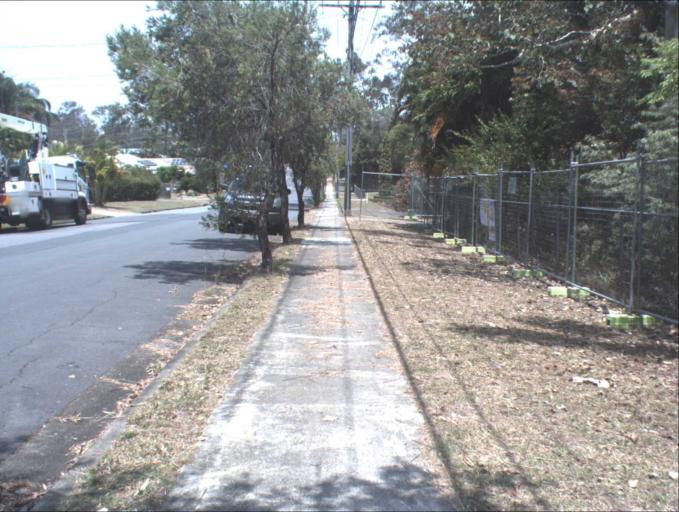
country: AU
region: Queensland
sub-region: Logan
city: Beenleigh
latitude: -27.6683
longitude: 153.1978
